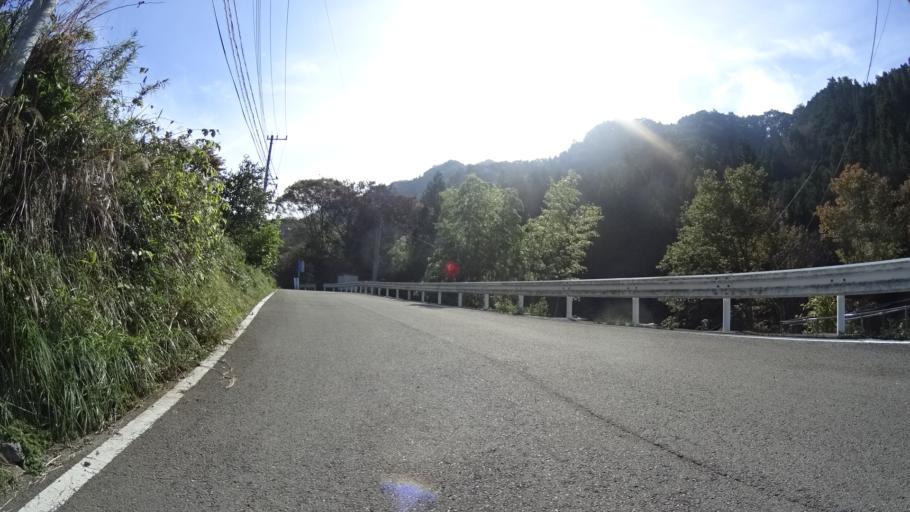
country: JP
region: Yamanashi
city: Otsuki
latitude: 35.5833
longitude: 138.9700
